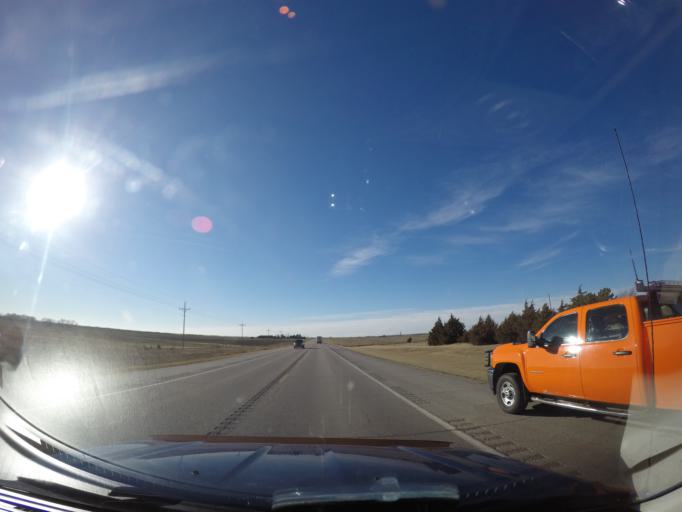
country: US
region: Kansas
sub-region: Marion County
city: Hillsboro
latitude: 38.3626
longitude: -97.2613
